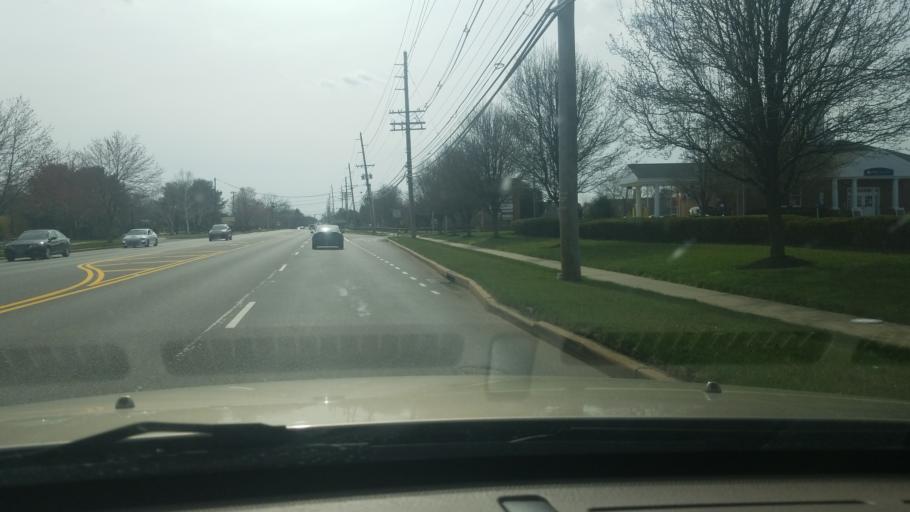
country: US
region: New Jersey
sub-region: Monmouth County
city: West Freehold
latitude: 40.2416
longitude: -74.3028
